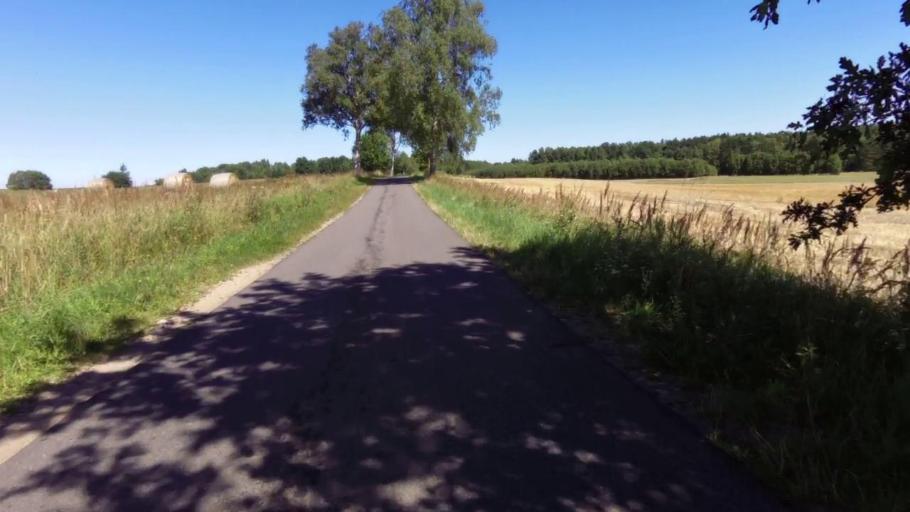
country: PL
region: West Pomeranian Voivodeship
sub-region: Powiat szczecinecki
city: Lubowo
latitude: 53.5690
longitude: 16.3601
